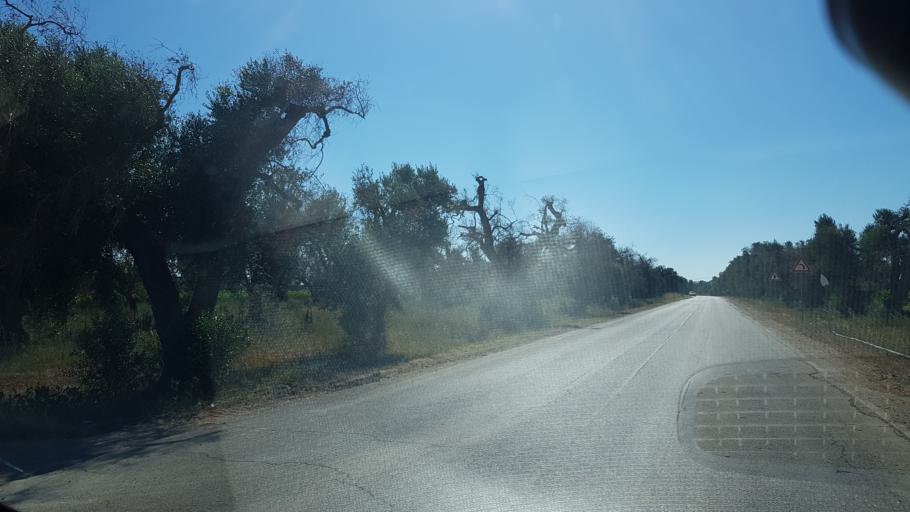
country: IT
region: Apulia
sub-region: Provincia di Brindisi
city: Tuturano
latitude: 40.5507
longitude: 17.8840
